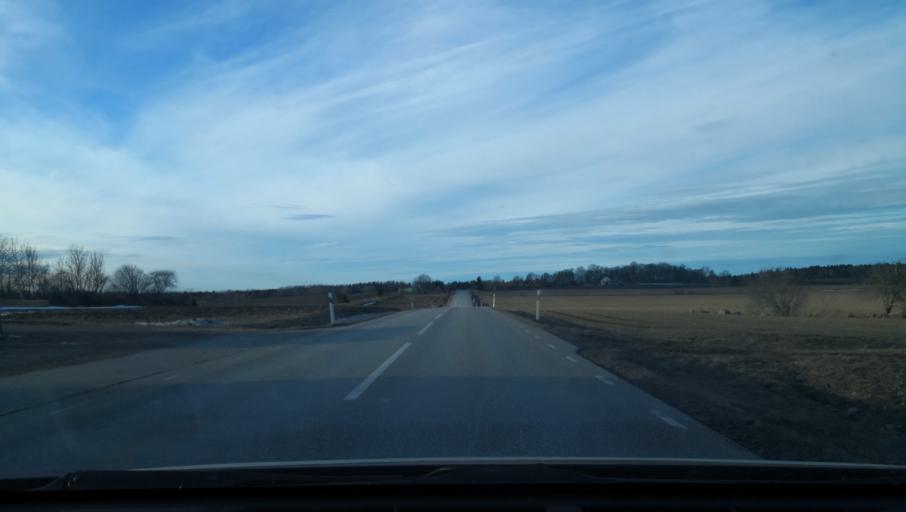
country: SE
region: Uppsala
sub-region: Osthammars Kommun
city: OEsthammar
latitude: 60.3130
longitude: 18.2656
